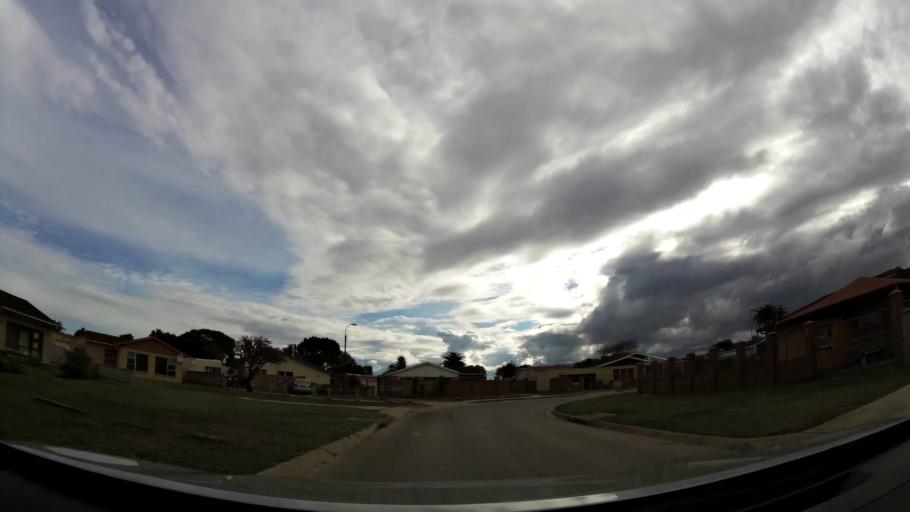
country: ZA
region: Eastern Cape
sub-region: Nelson Mandela Bay Metropolitan Municipality
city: Port Elizabeth
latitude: -33.9374
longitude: 25.4739
